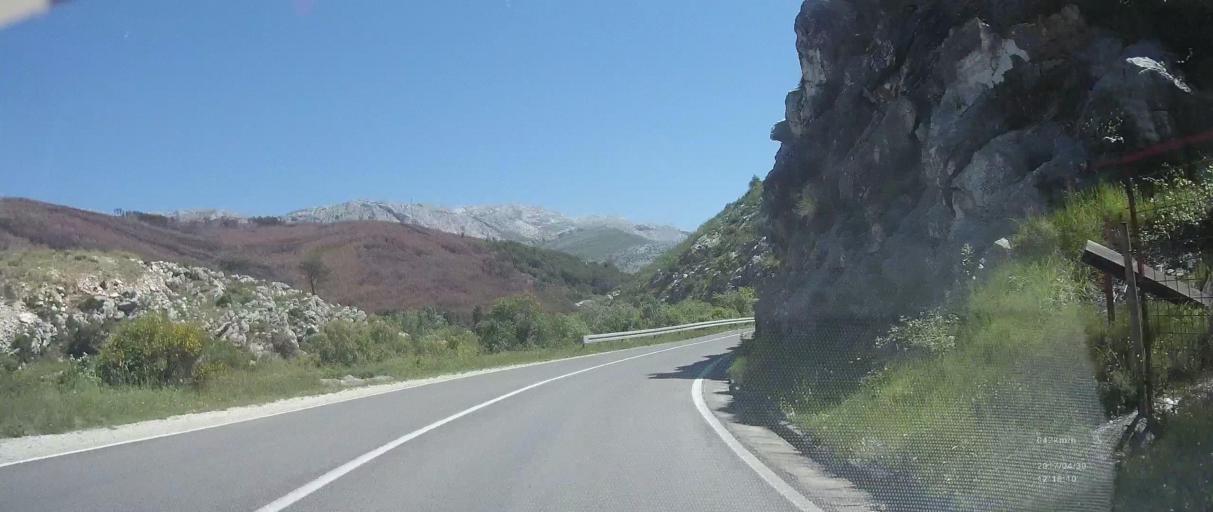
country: HR
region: Splitsko-Dalmatinska
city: Zrnovnica
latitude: 43.5185
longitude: 16.5441
